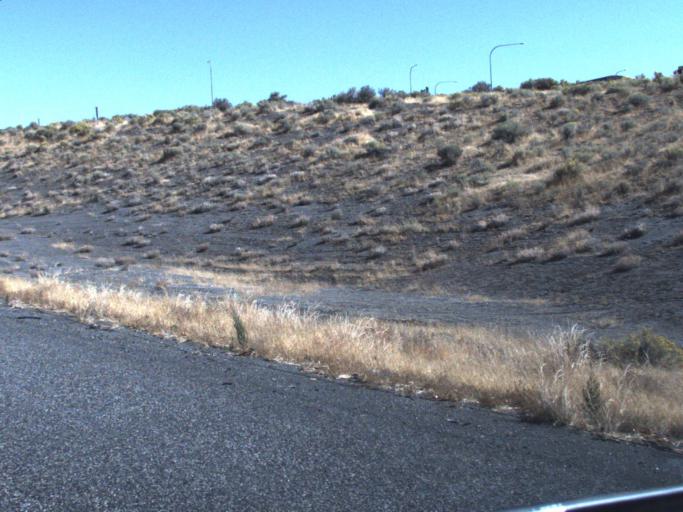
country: US
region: Washington
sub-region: Franklin County
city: West Pasco
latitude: 46.2746
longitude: -119.2238
